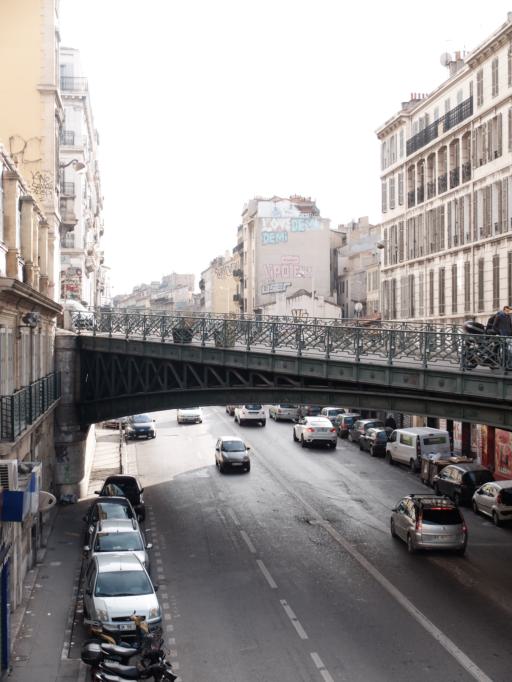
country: FR
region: Provence-Alpes-Cote d'Azur
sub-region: Departement des Bouches-du-Rhone
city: Marseille
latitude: 43.2934
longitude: 5.3824
